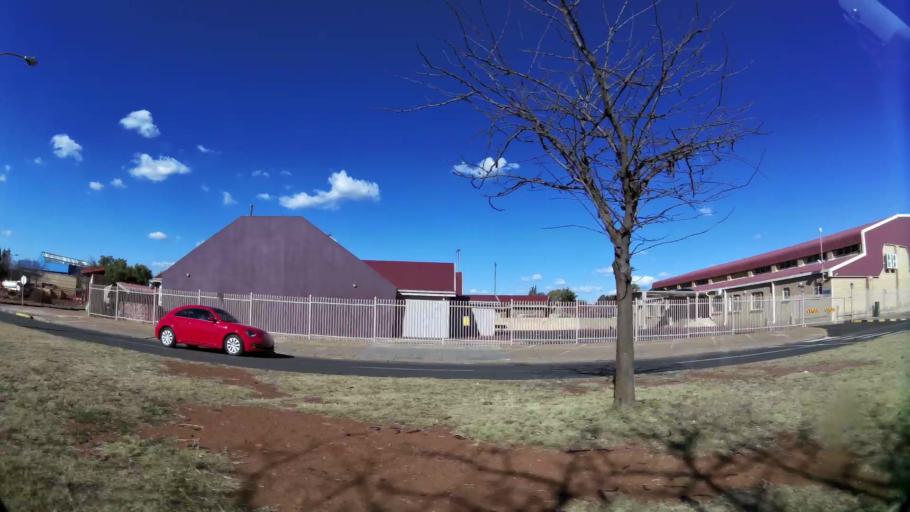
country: ZA
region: Gauteng
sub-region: West Rand District Municipality
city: Carletonville
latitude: -26.3610
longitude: 27.3816
